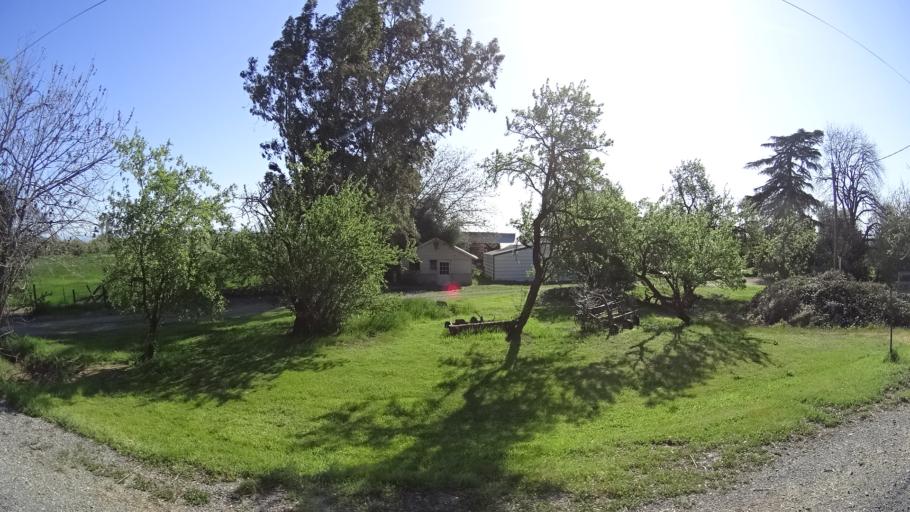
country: US
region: California
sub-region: Glenn County
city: Hamilton City
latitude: 39.7833
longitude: -122.0665
